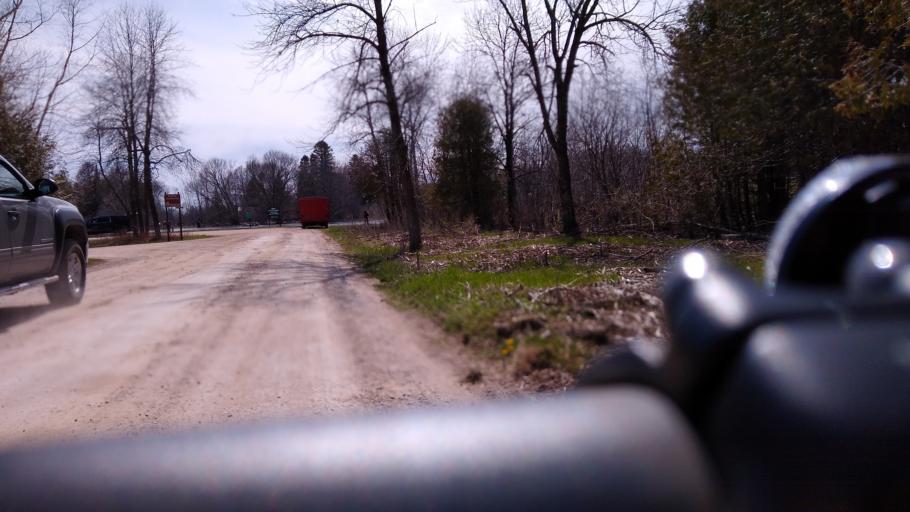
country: US
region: Michigan
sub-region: Delta County
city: Escanaba
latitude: 45.6779
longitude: -87.1414
